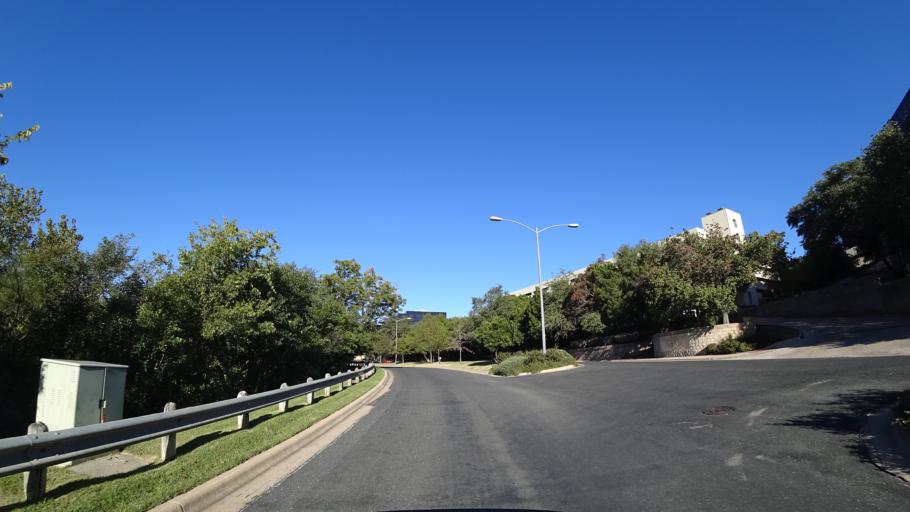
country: US
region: Texas
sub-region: Travis County
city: West Lake Hills
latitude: 30.3537
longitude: -97.7995
